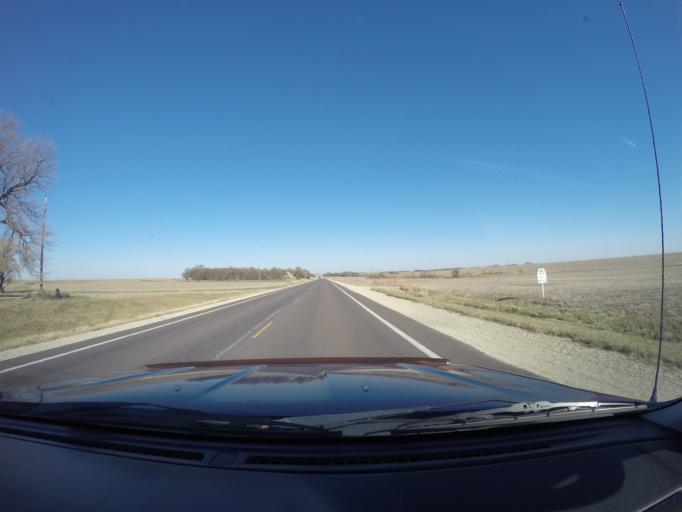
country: US
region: Kansas
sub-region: Marshall County
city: Blue Rapids
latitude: 39.6151
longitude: -96.7501
